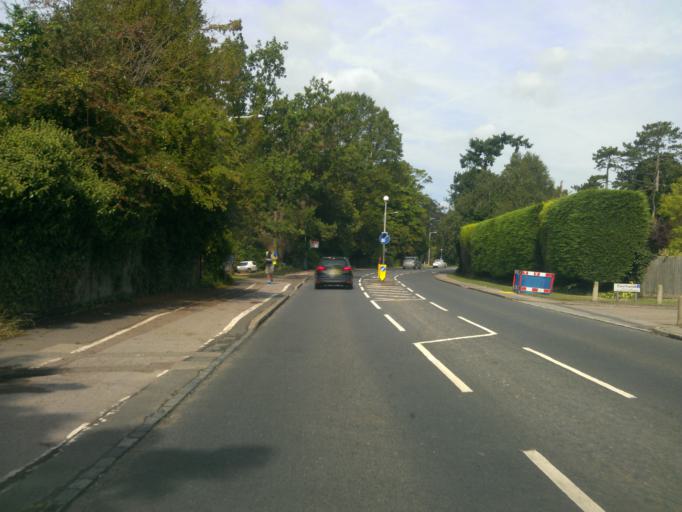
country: GB
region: England
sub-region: Kent
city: Tonbridge
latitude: 51.2040
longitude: 0.2670
